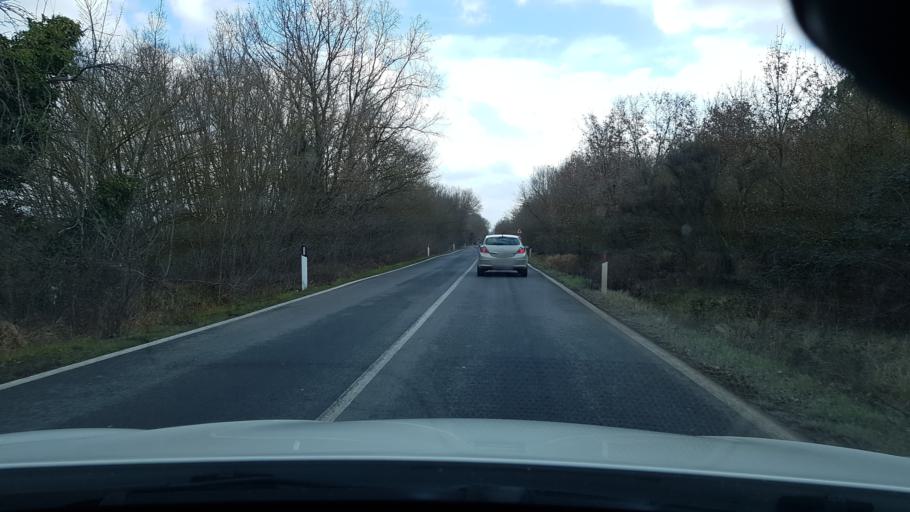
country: IT
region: Umbria
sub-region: Provincia di Perugia
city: Castiglione del Lago
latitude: 43.1316
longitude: 12.0300
